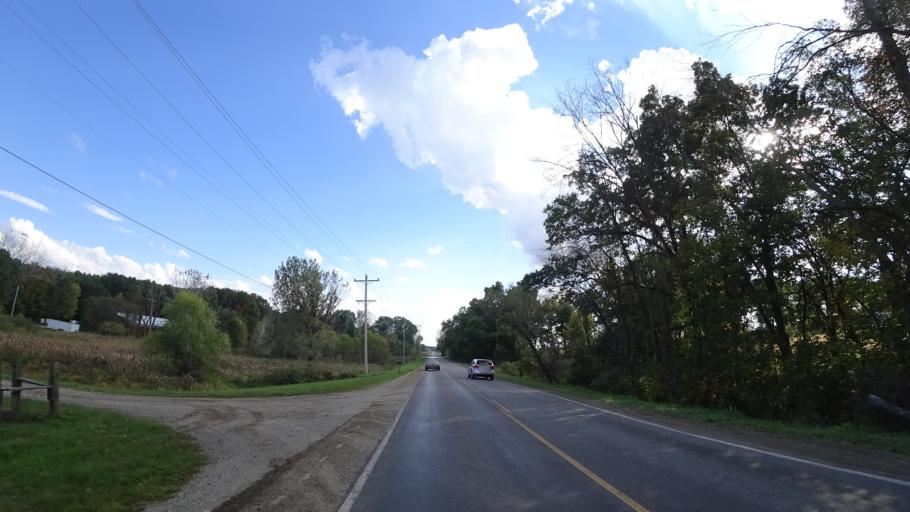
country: US
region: Michigan
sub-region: Saint Joseph County
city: Centreville
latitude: 41.9497
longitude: -85.5278
